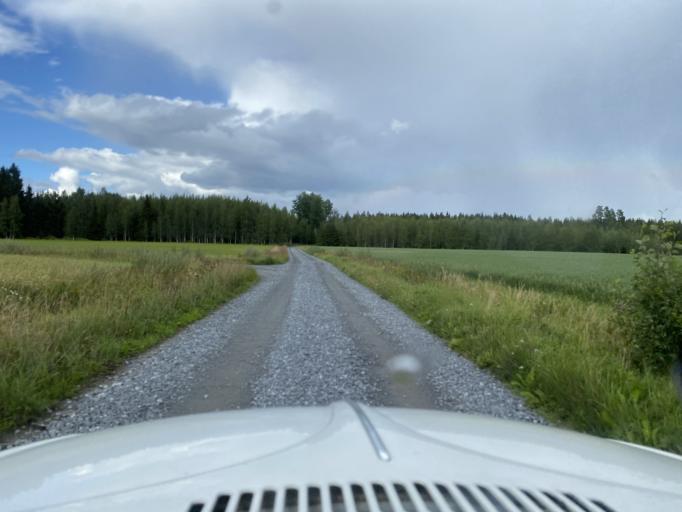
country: FI
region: Pirkanmaa
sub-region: Lounais-Pirkanmaa
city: Punkalaidun
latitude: 61.1332
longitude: 23.0671
